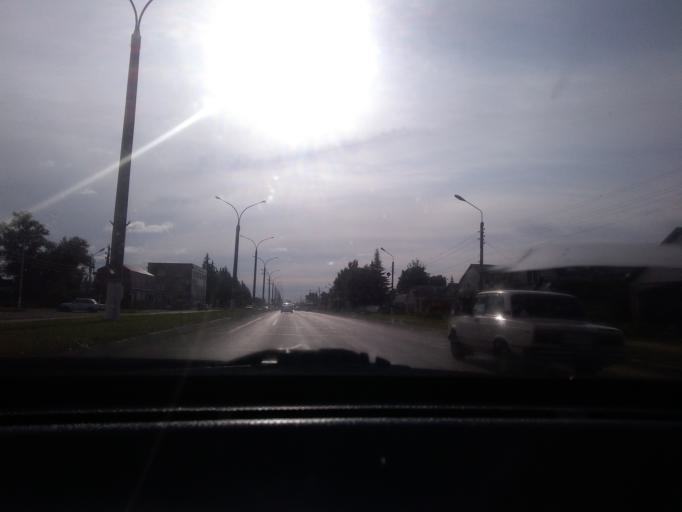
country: RU
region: Kursk
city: Pryamitsyno
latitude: 51.6569
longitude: 35.9361
